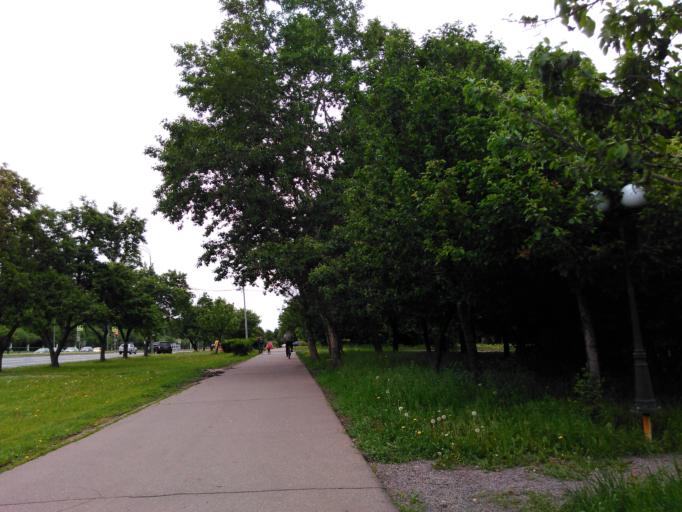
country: RU
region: Moskovskaya
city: Semenovskoye
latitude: 55.6966
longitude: 37.5413
